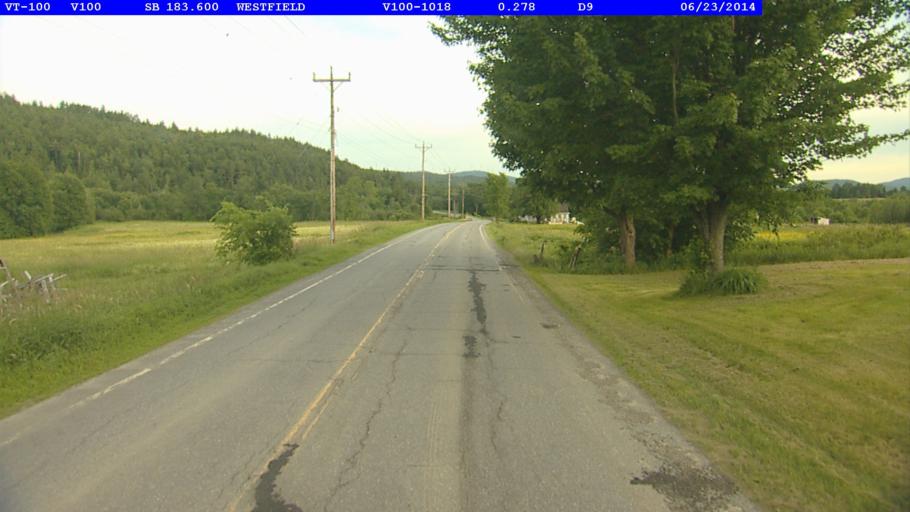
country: US
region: Vermont
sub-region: Orleans County
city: Newport
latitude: 44.8389
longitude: -72.4339
